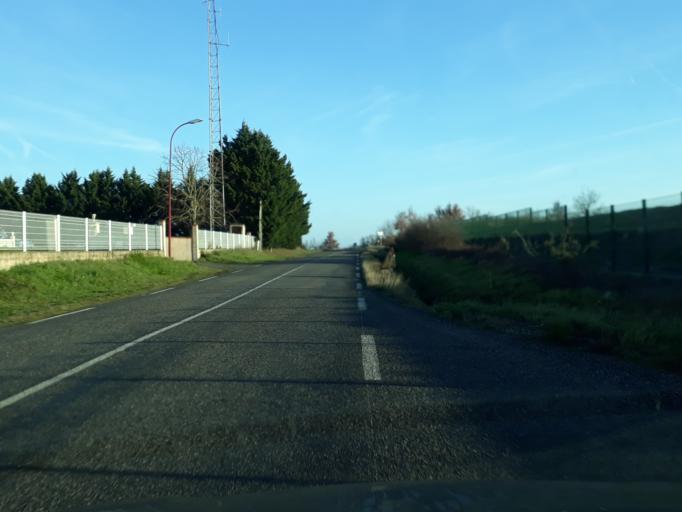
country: FR
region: Midi-Pyrenees
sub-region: Departement du Gers
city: Pujaudran
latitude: 43.5797
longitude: 1.1320
